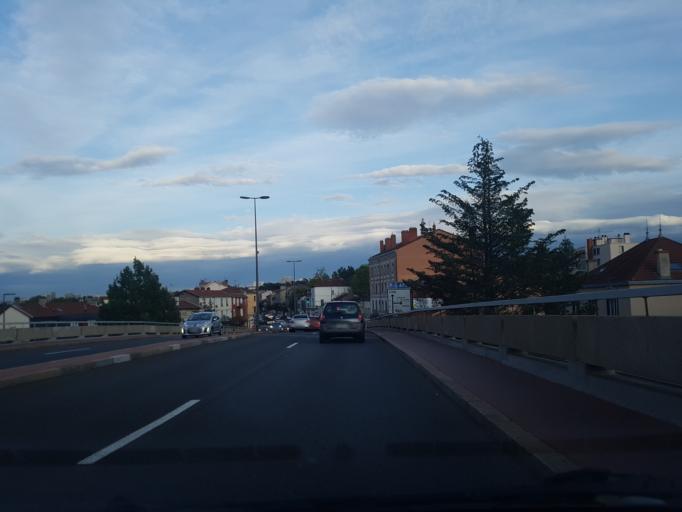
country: FR
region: Rhone-Alpes
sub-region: Departement du Rhone
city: Ecully
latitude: 45.7638
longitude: 4.7715
